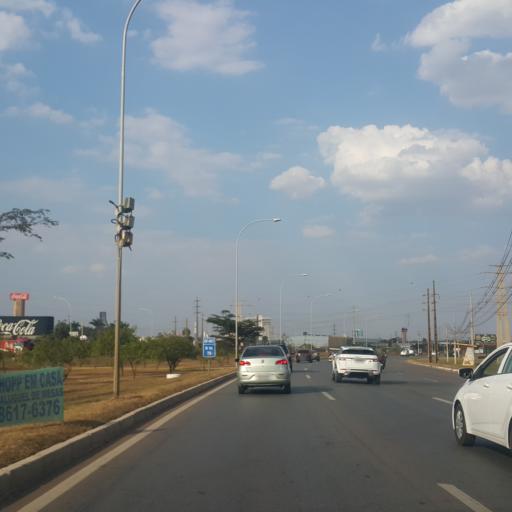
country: BR
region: Federal District
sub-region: Brasilia
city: Brasilia
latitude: -15.8742
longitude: -48.0445
